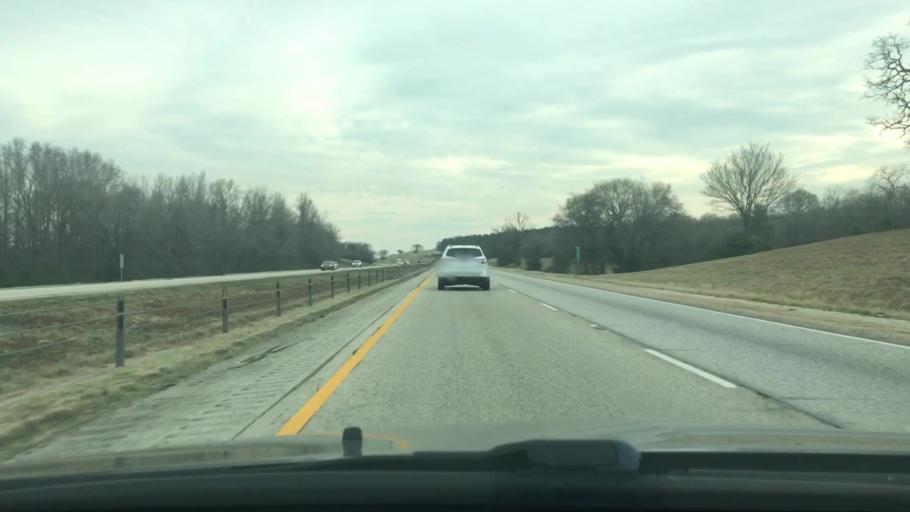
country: US
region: Texas
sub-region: Leon County
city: Centerville
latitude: 31.2989
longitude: -95.9994
